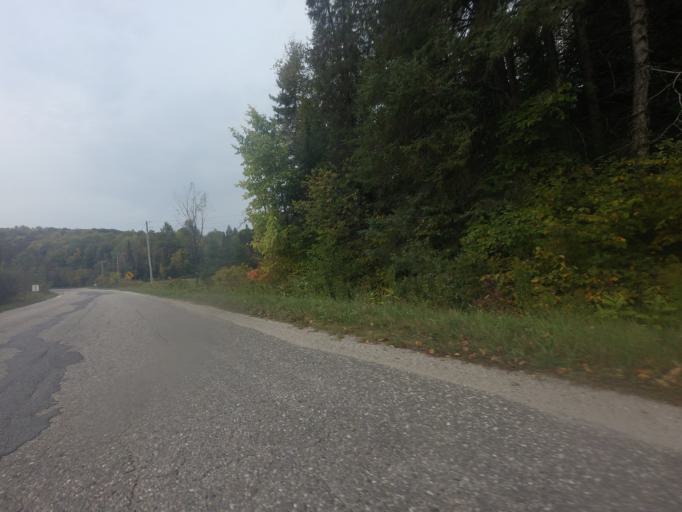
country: CA
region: Quebec
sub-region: Outaouais
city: Maniwaki
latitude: 46.0880
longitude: -76.0331
